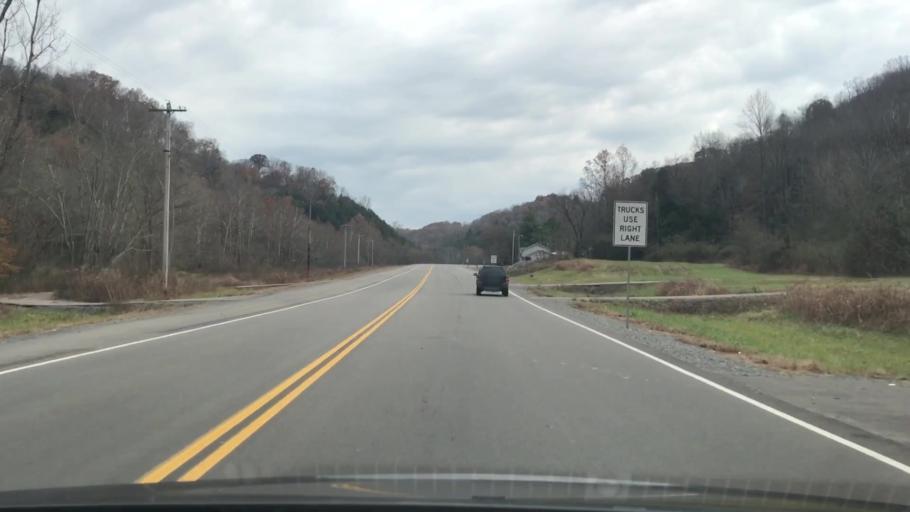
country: US
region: Tennessee
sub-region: Macon County
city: Lafayette
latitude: 36.4982
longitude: -86.0497
